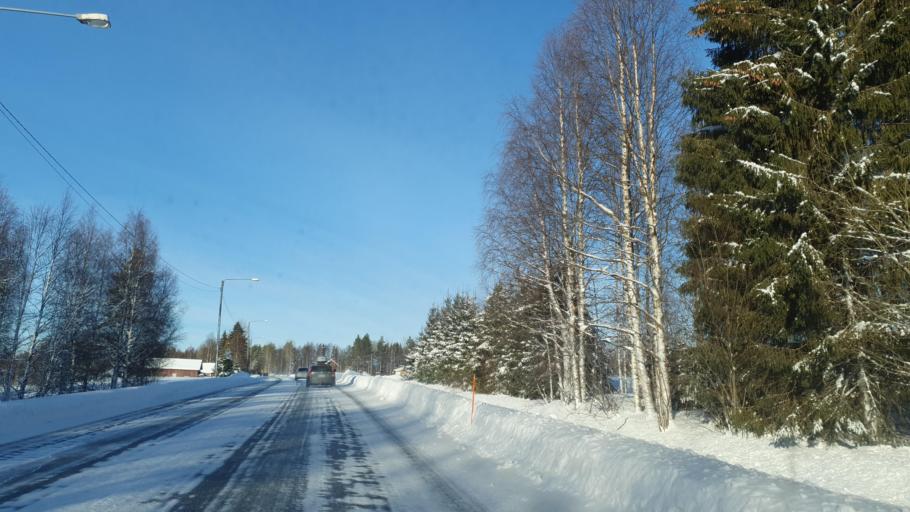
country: FI
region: Lapland
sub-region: Kemi-Tornio
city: Tornio
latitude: 66.0778
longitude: 23.9789
